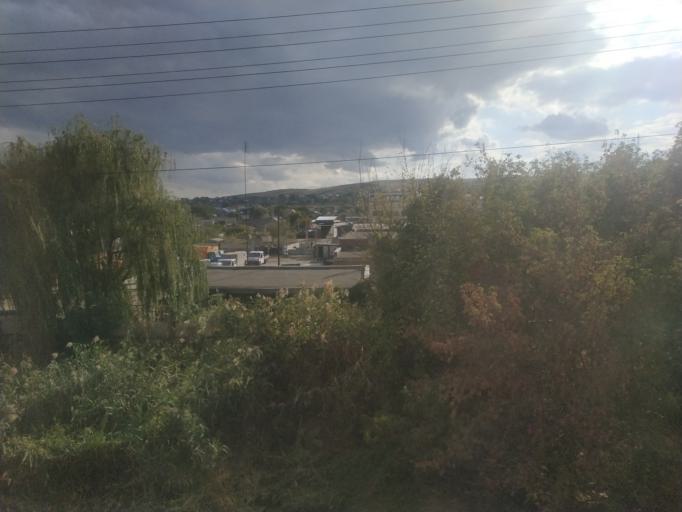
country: RU
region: Volgograd
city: Krasnoslobodsk
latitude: 48.5072
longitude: 44.5456
